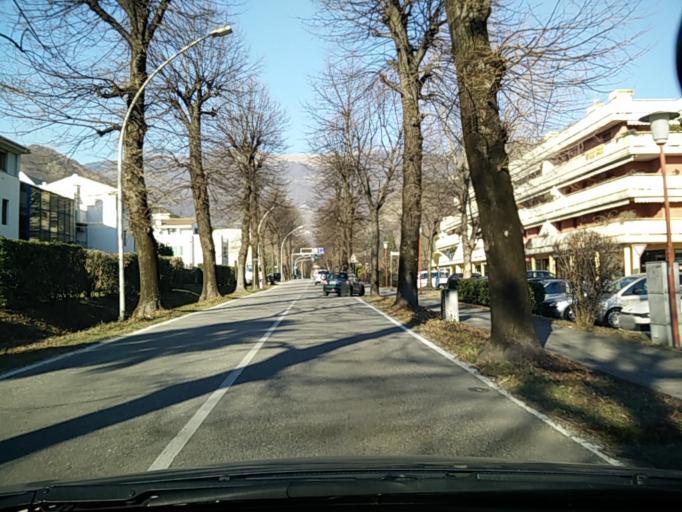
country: IT
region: Veneto
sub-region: Provincia di Treviso
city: Vittorio Veneto
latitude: 45.9933
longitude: 12.2965
